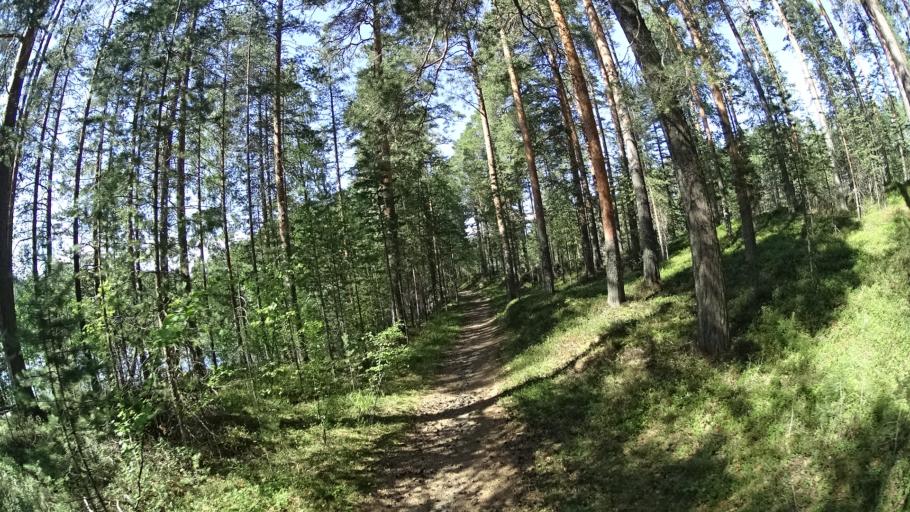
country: FI
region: Southern Savonia
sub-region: Savonlinna
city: Punkaharju
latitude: 61.7723
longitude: 29.3452
